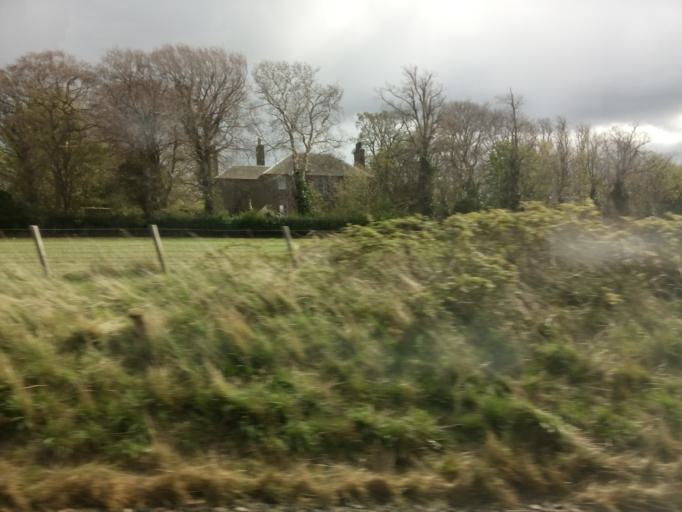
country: GB
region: Scotland
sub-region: East Lothian
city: Gullane
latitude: 56.0005
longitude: -2.8102
